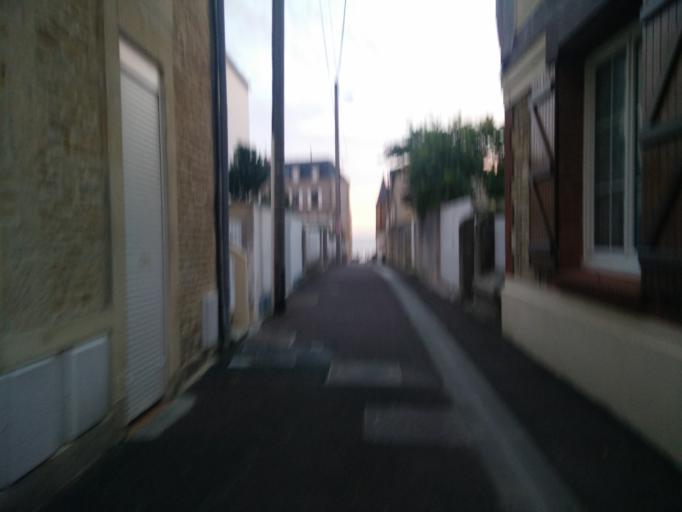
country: FR
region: Lower Normandy
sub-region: Departement du Calvados
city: Saint-Aubin-sur-Mer
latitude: 49.3310
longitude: -0.3928
